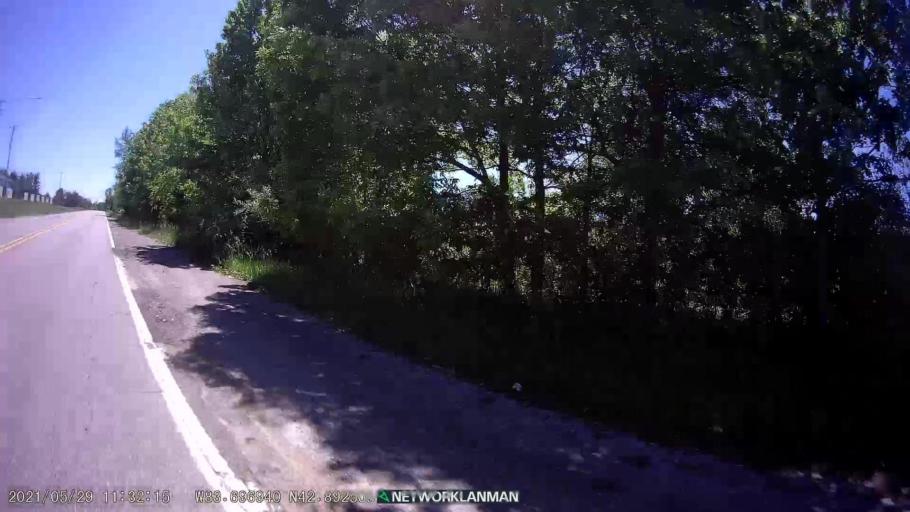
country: US
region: Michigan
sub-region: Genesee County
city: Lake Fenton
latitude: 42.8922
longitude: -83.6970
